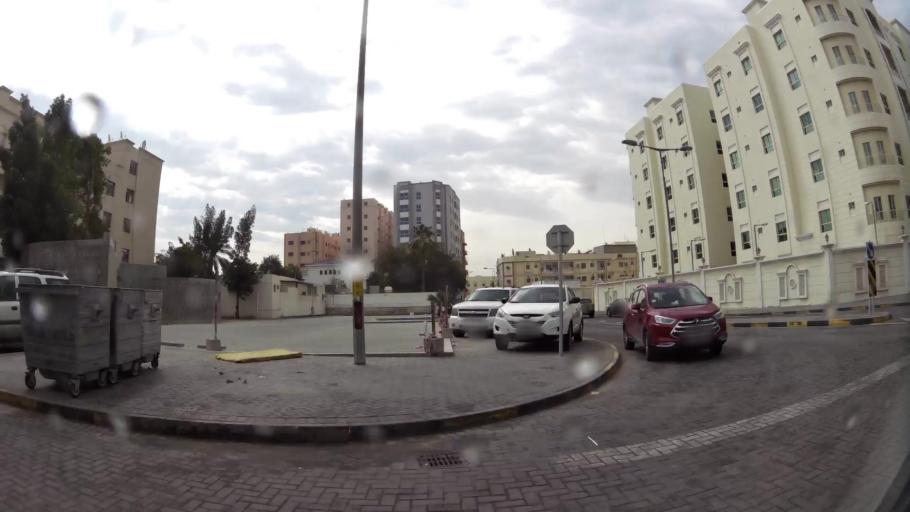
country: BH
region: Manama
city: Manama
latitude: 26.2257
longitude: 50.5938
